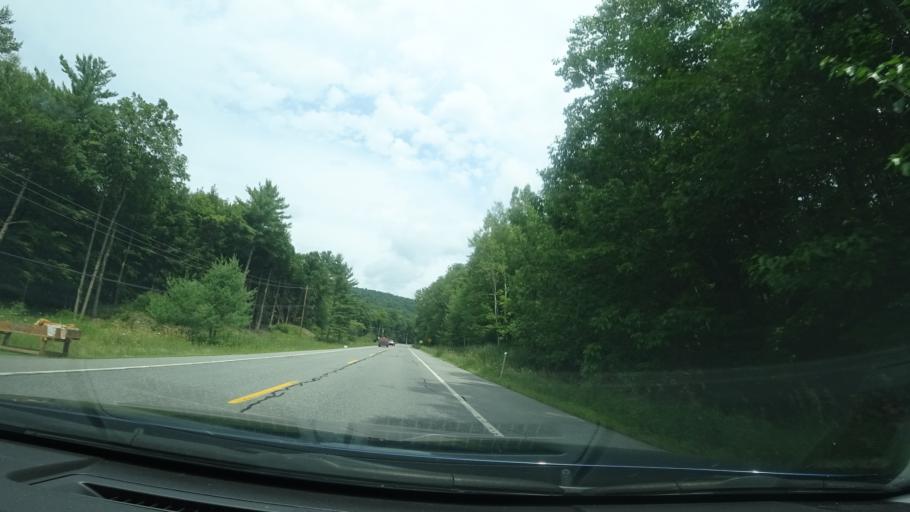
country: US
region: New York
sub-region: Washington County
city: Whitehall
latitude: 43.6386
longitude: -73.4462
